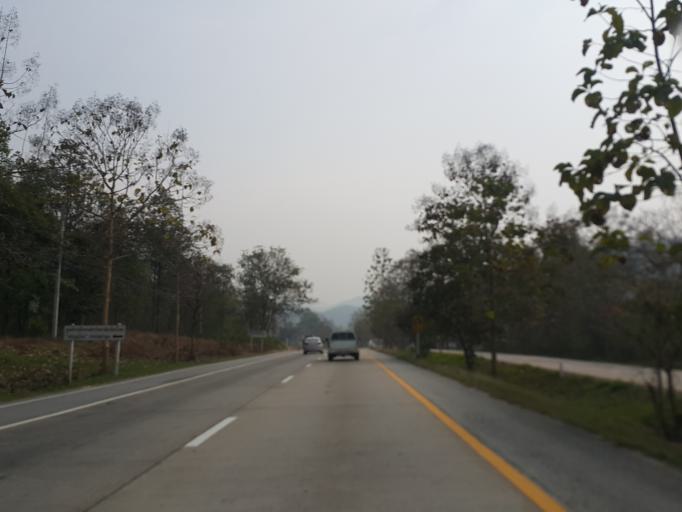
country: TH
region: Lamphun
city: Mae Tha
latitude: 18.5082
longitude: 99.1038
